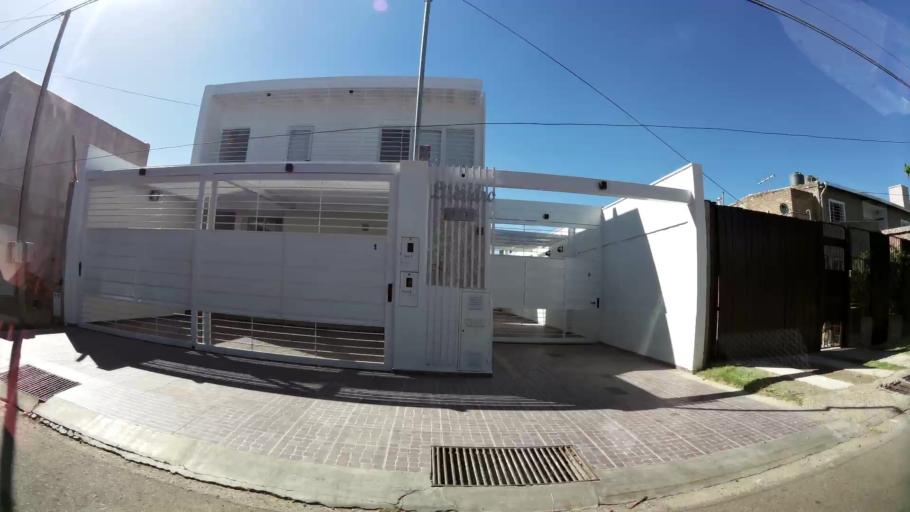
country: AR
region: Mendoza
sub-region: Departamento de Maipu
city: Maipu
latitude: -32.9741
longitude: -68.7988
